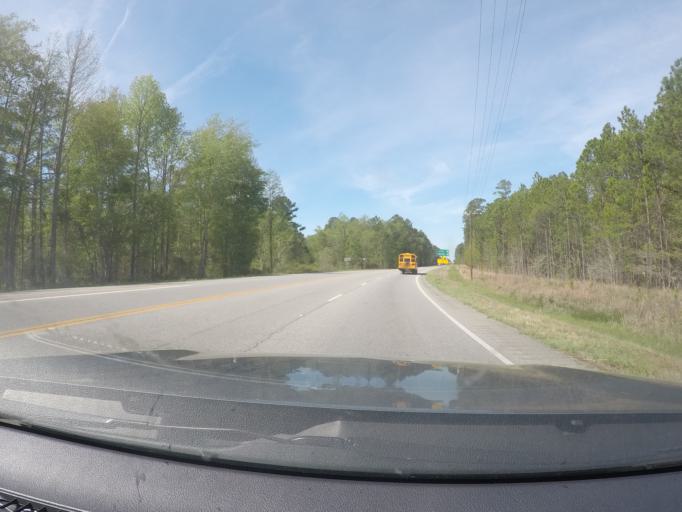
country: US
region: Georgia
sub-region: Bryan County
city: Pembroke
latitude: 32.1302
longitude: -81.5408
